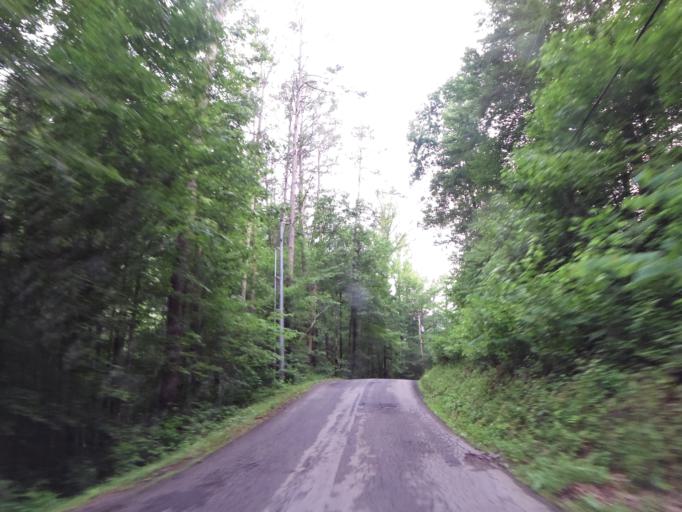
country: US
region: Tennessee
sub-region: Blount County
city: Wildwood
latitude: 35.7425
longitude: -83.7742
